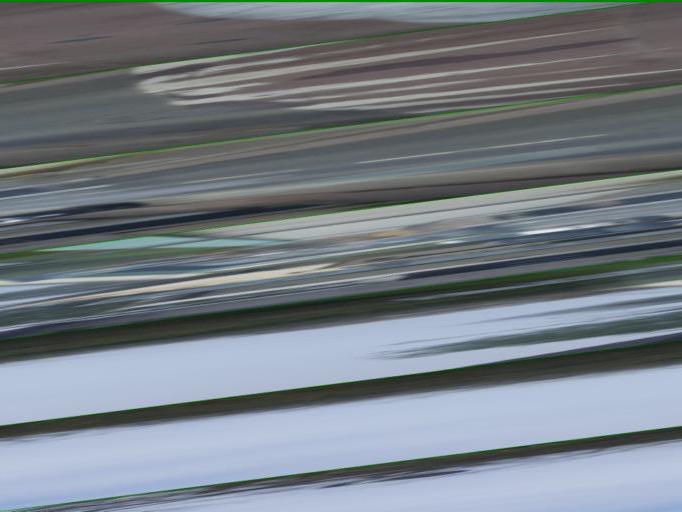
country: FR
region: Ile-de-France
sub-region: Departement des Yvelines
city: Houdan
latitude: 48.7956
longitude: 1.6004
